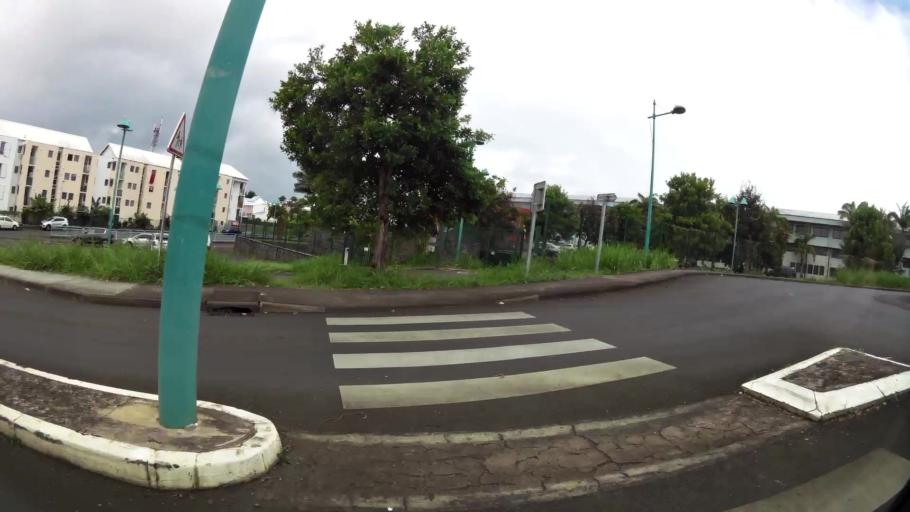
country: RE
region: Reunion
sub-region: Reunion
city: Sainte-Suzanne
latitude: -20.9049
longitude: 55.6003
